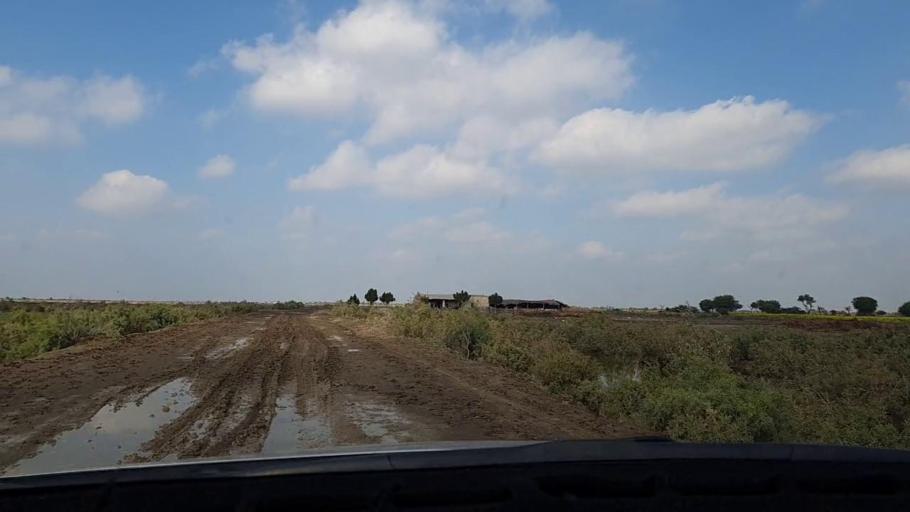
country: PK
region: Sindh
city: Tando Mittha Khan
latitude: 25.7825
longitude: 69.2560
